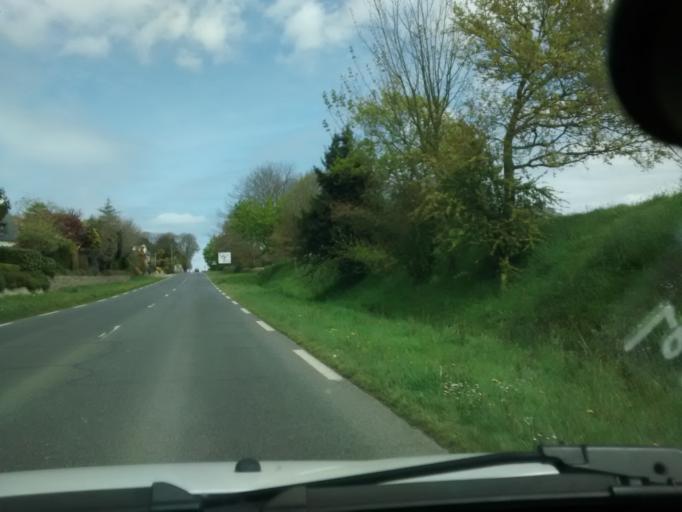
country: FR
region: Brittany
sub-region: Departement des Cotes-d'Armor
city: Minihy-Treguier
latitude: 48.7763
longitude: -3.2356
